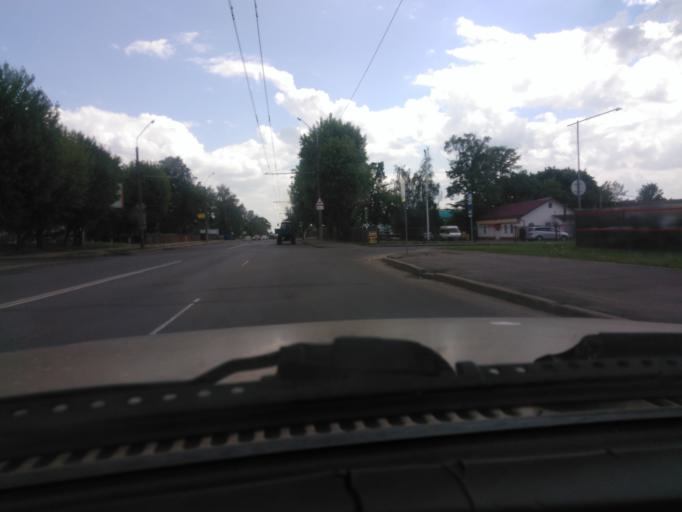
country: BY
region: Mogilev
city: Mahilyow
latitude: 53.9338
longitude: 30.3356
